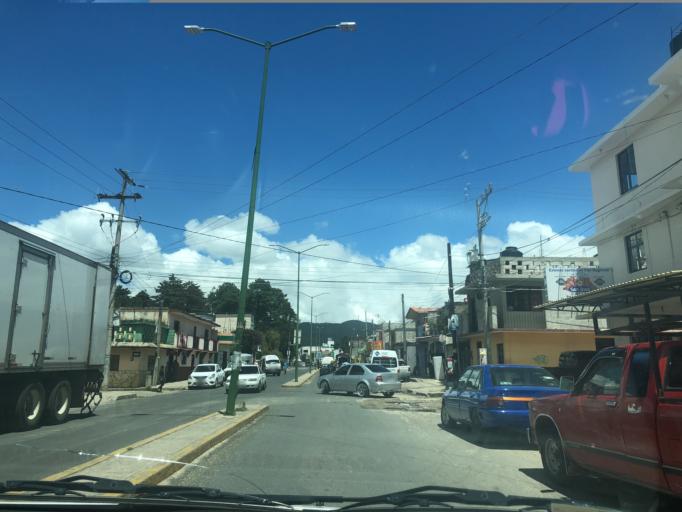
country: MX
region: Chiapas
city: San Cristobal de las Casas
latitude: 16.7198
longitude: -92.6400
